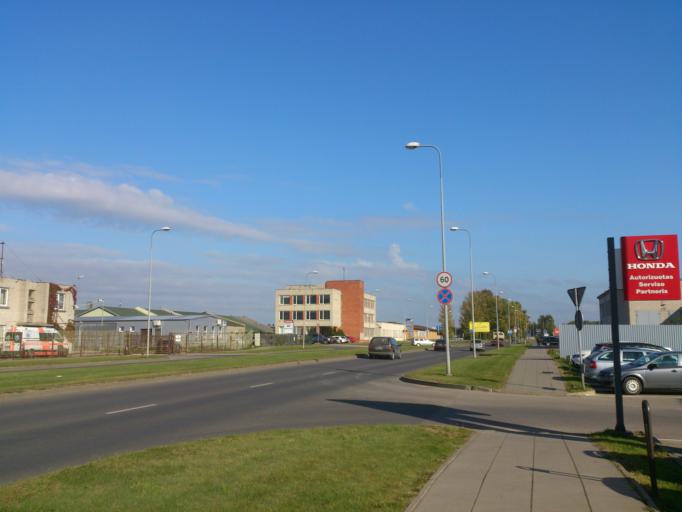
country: LT
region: Kauno apskritis
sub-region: Kaunas
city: Aleksotas
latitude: 54.8751
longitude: 23.8985
